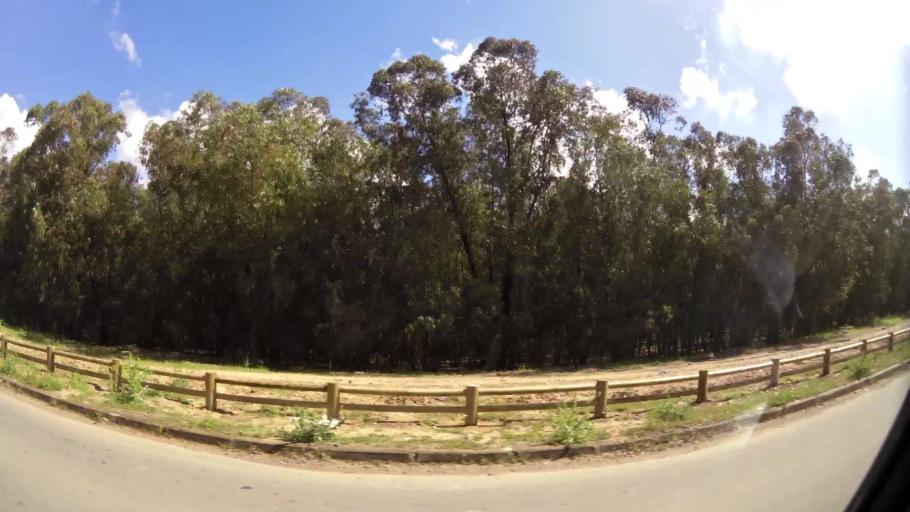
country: MA
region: Grand Casablanca
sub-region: Nouaceur
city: Bouskoura
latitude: 33.4805
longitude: -7.5872
